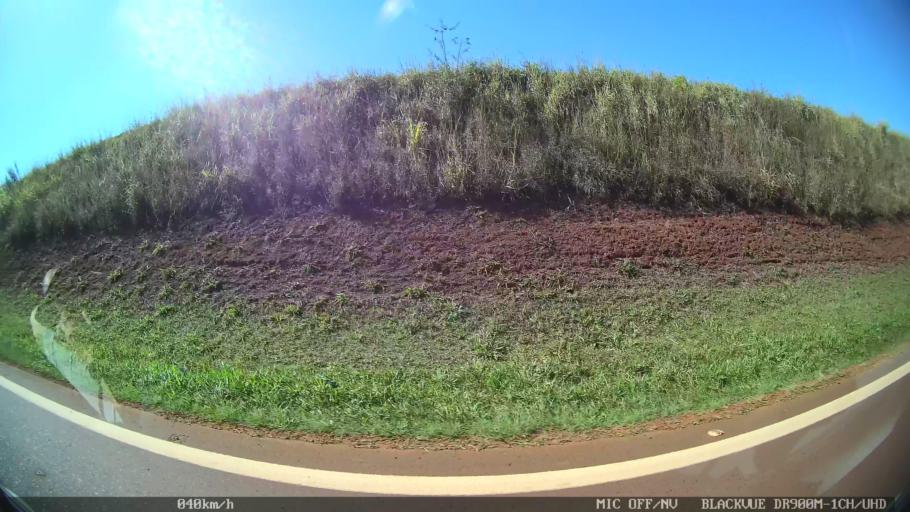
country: BR
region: Sao Paulo
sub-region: Franca
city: Franca
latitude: -20.6759
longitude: -47.4952
